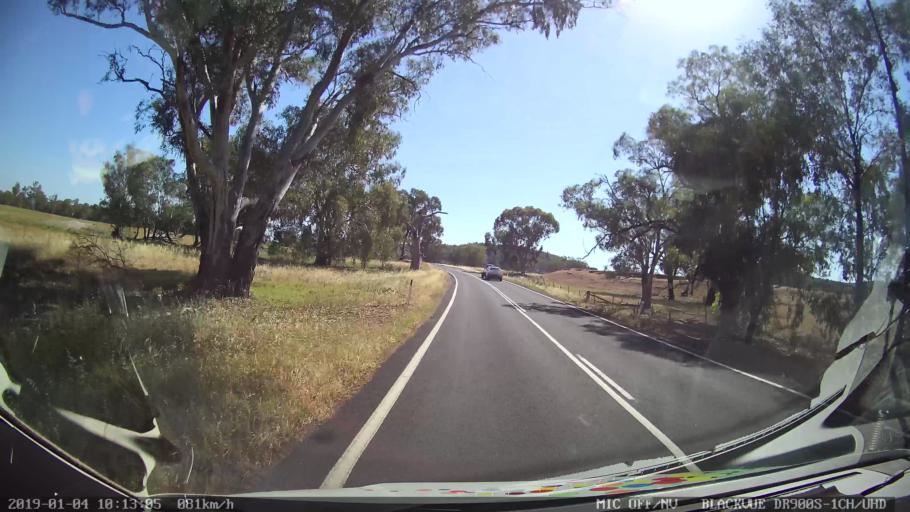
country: AU
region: New South Wales
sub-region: Cabonne
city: Canowindra
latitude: -33.4097
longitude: 148.4030
